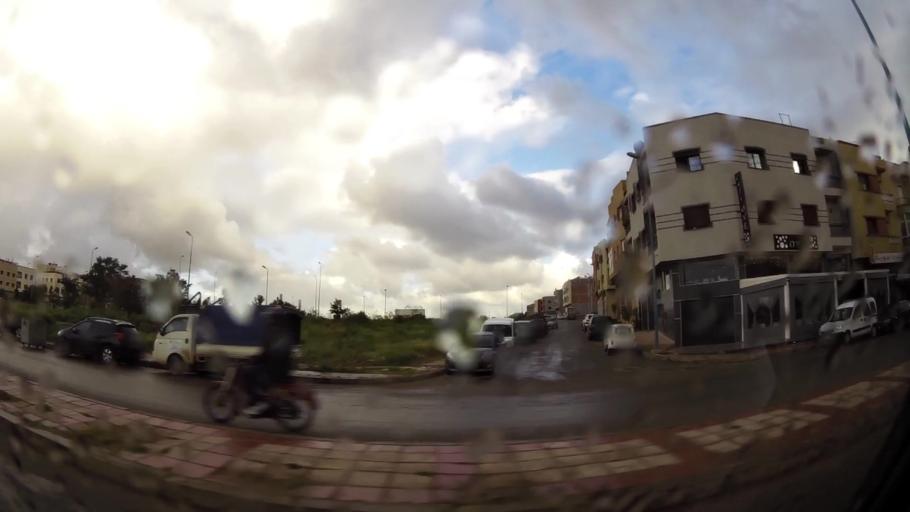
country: MA
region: Grand Casablanca
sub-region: Mohammedia
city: Mohammedia
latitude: 33.6807
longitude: -7.3842
